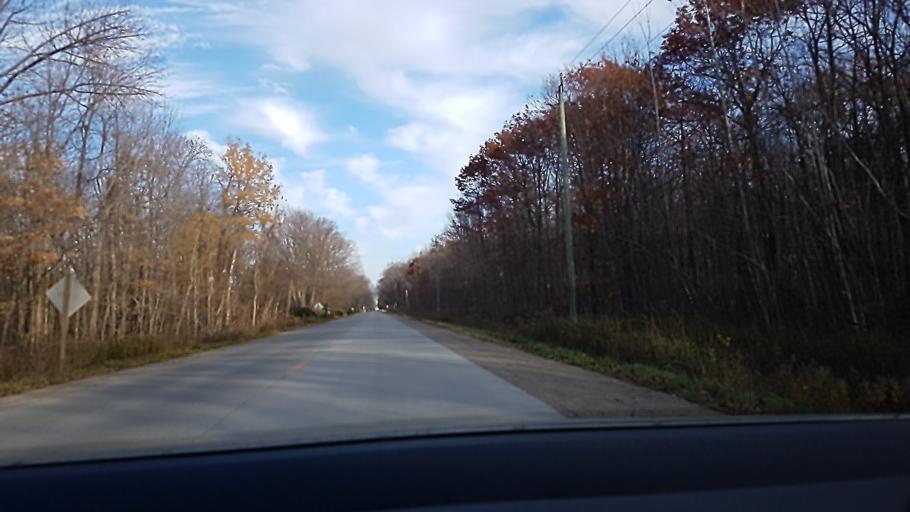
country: CA
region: Ontario
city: Barrie
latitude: 44.3970
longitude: -79.5282
